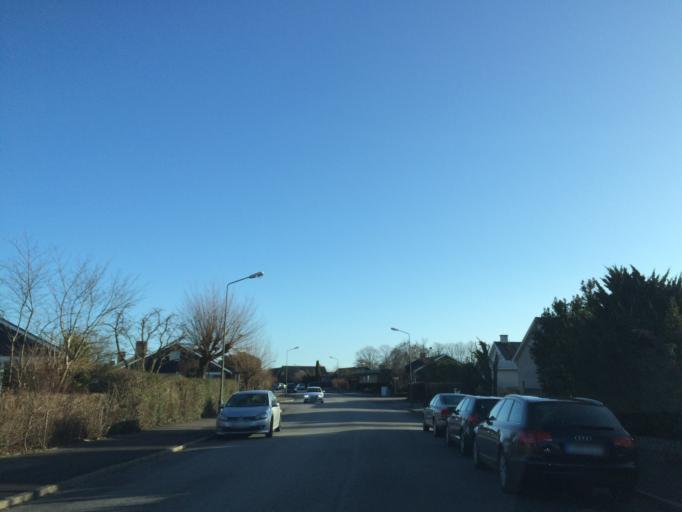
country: SE
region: Skane
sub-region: Malmo
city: Bunkeflostrand
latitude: 55.5732
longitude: 12.9557
